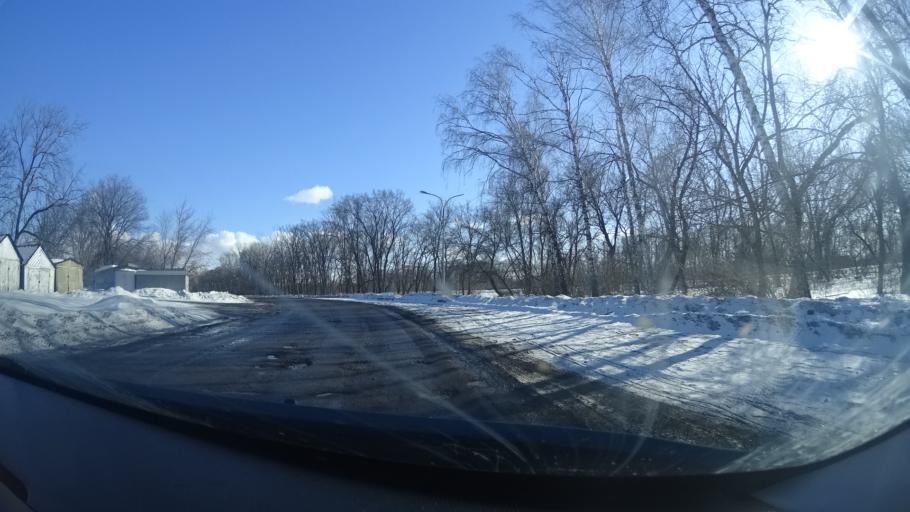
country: RU
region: Bashkortostan
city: Chishmy
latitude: 54.5850
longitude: 55.3709
